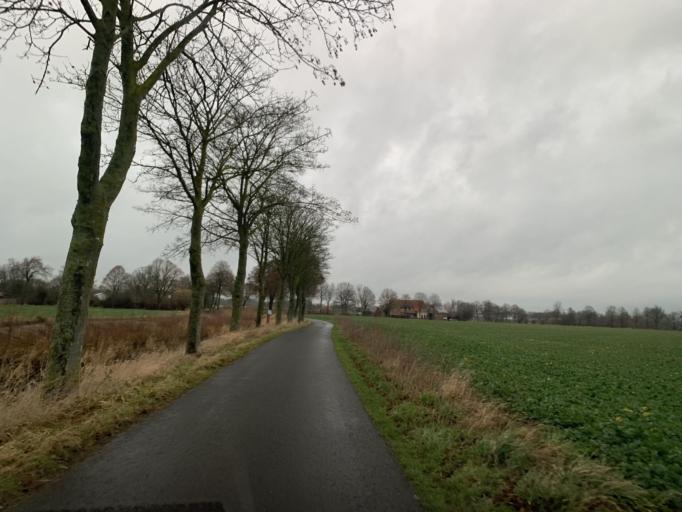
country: DE
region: North Rhine-Westphalia
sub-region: Regierungsbezirk Munster
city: Nordwalde
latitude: 52.0991
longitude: 7.4833
